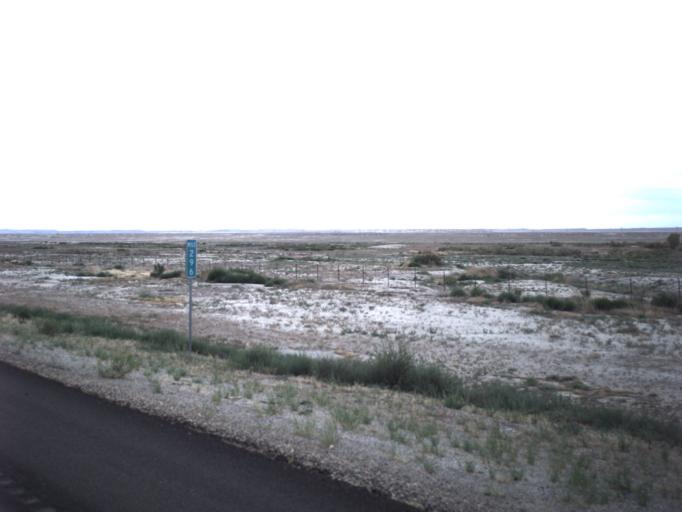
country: US
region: Utah
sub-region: Carbon County
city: East Carbon City
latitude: 39.0174
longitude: -110.2901
